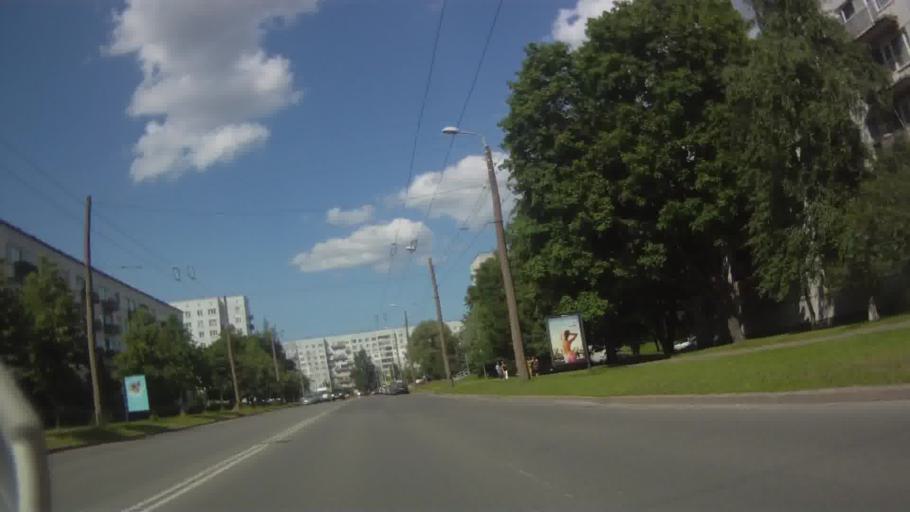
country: LV
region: Riga
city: Riga
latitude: 56.9567
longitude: 24.1764
